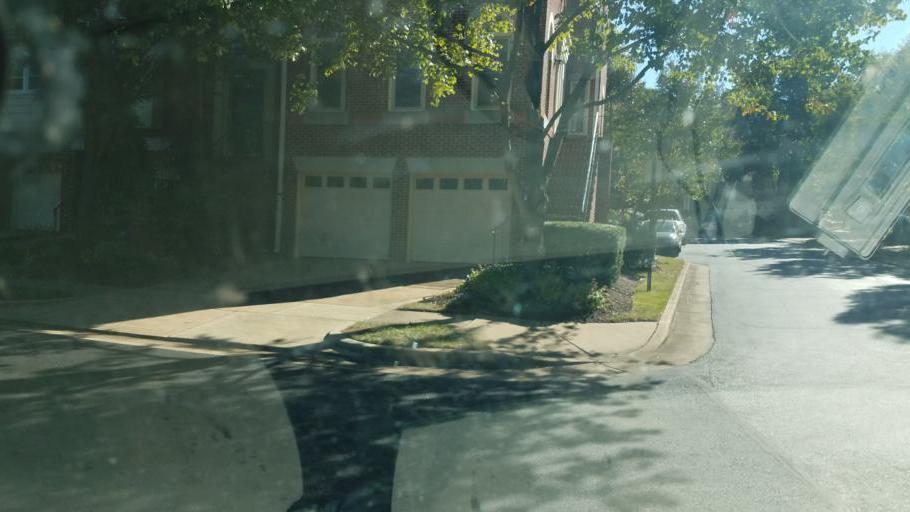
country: US
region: Virginia
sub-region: City of Alexandria
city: Alexandria
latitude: 38.8408
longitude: -77.0667
